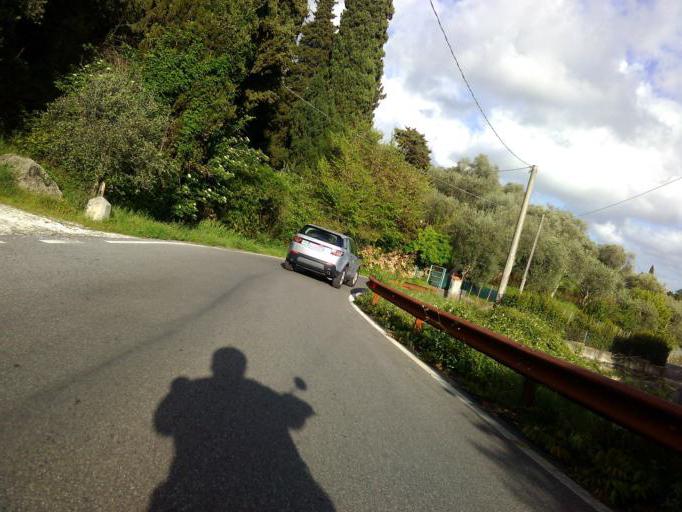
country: IT
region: Tuscany
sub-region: Provincia di Lucca
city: Piano di Mommio
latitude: 43.9513
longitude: 10.2708
